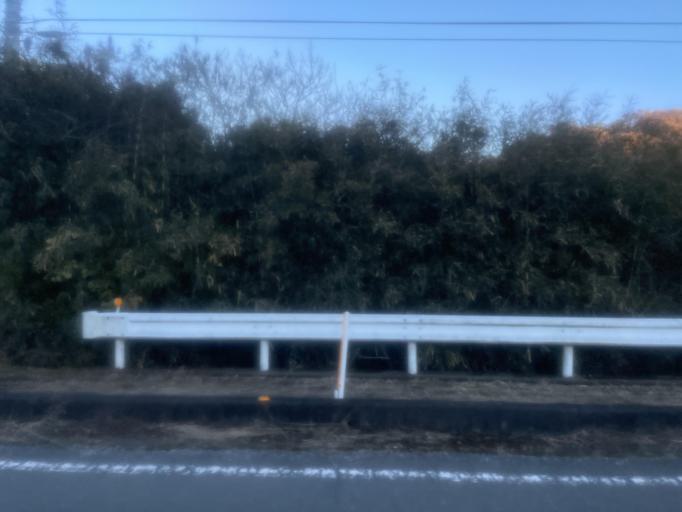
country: JP
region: Saitama
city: Yorii
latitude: 36.0963
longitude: 139.1758
